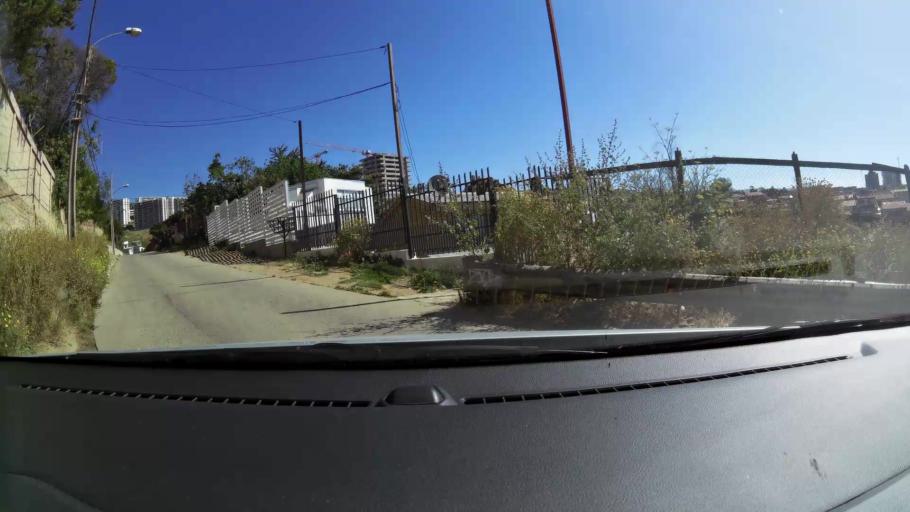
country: CL
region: Valparaiso
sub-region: Provincia de Valparaiso
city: Vina del Mar
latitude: -33.0319
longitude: -71.5728
